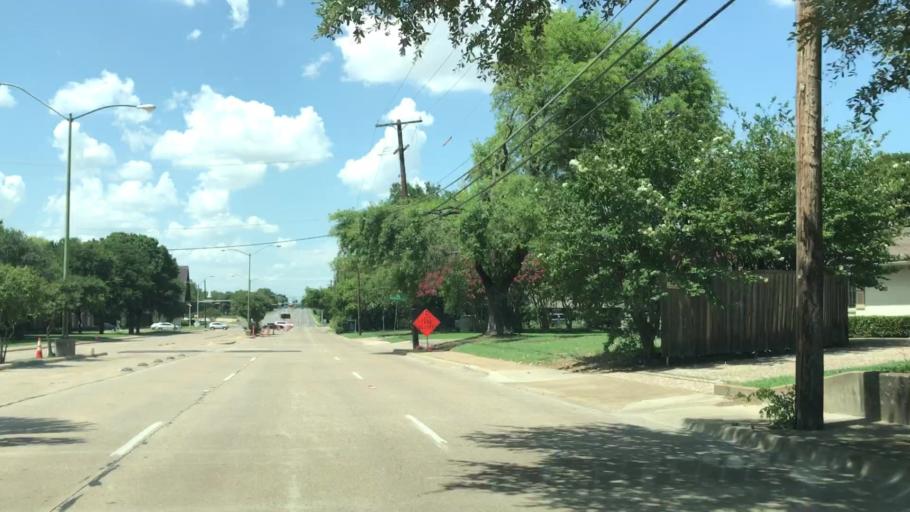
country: US
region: Texas
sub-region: Dallas County
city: University Park
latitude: 32.8932
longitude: -96.8383
